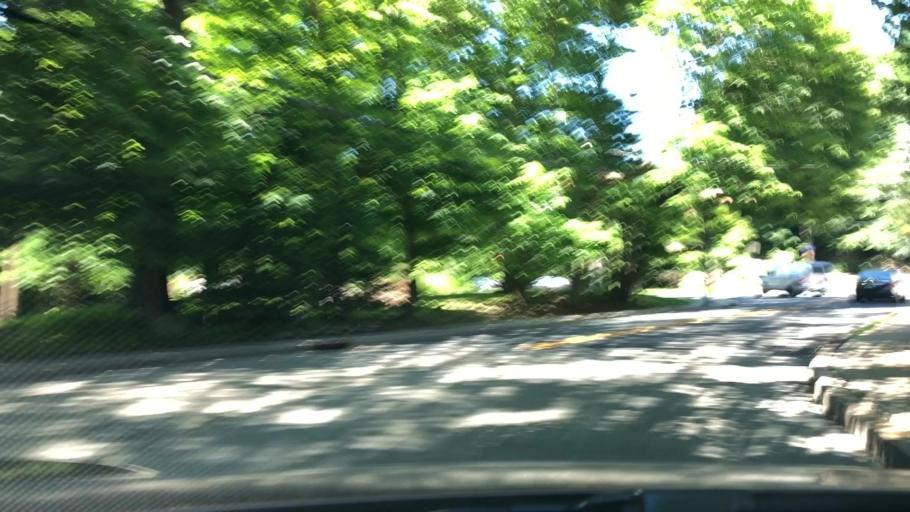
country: US
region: New York
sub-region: Westchester County
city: White Plains
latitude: 41.0317
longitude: -73.7767
